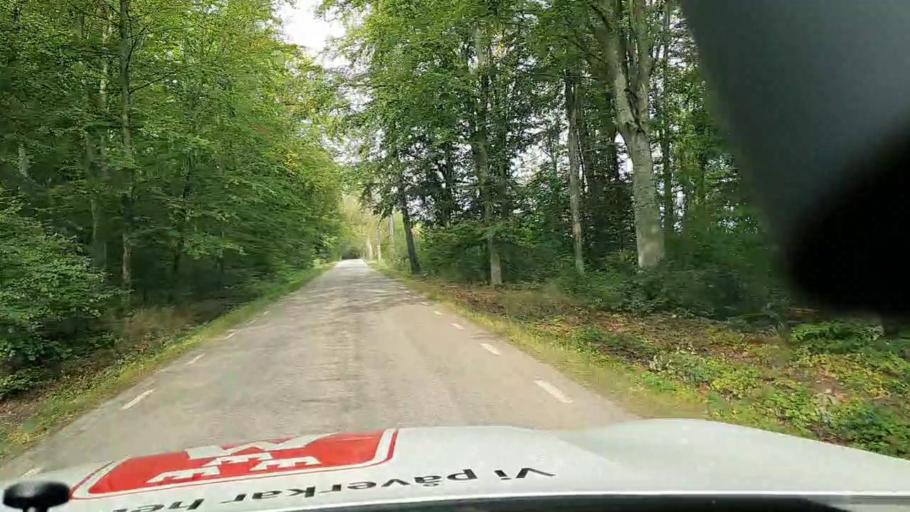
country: SE
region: Soedermanland
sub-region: Nykopings Kommun
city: Svalsta
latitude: 58.8278
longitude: 16.8851
